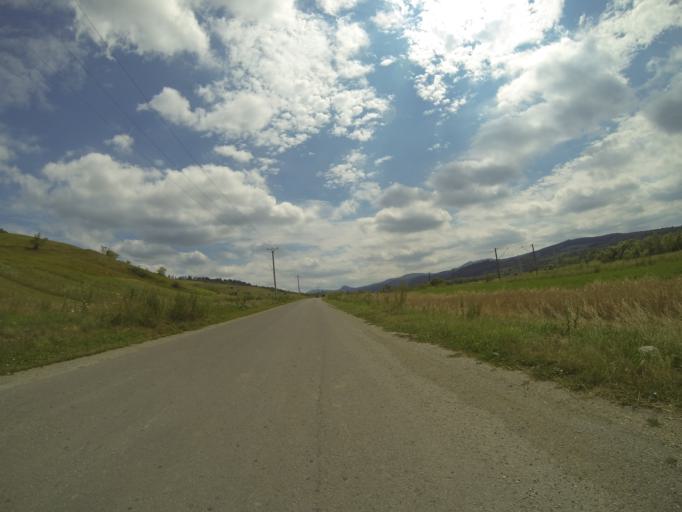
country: RO
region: Brasov
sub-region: Comuna Hoghiz
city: Hoghiz
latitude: 46.0289
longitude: 25.3827
